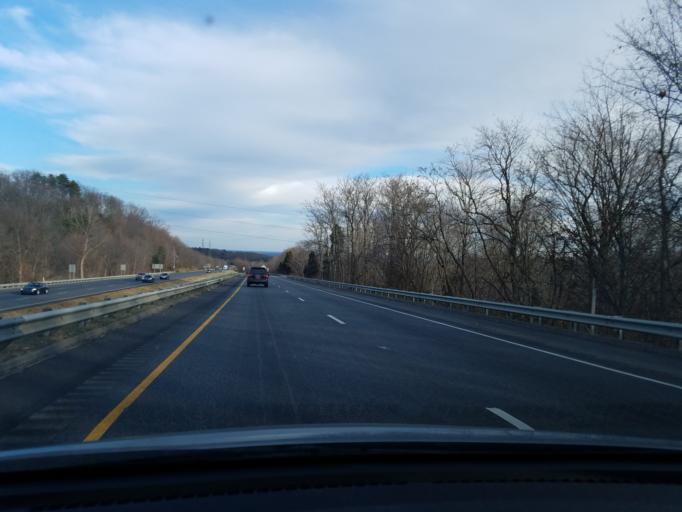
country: US
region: Indiana
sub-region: Floyd County
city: New Albany
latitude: 38.3013
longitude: -85.8639
